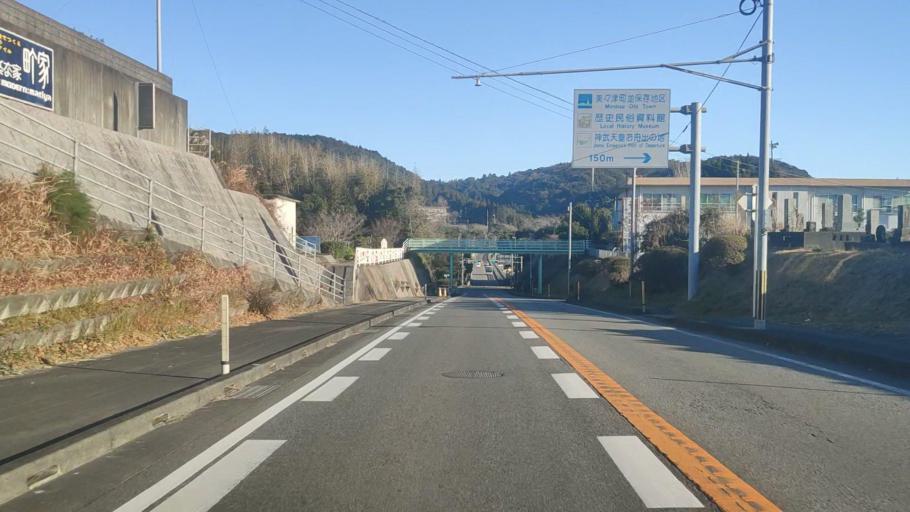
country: JP
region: Miyazaki
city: Takanabe
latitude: 32.3366
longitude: 131.6106
